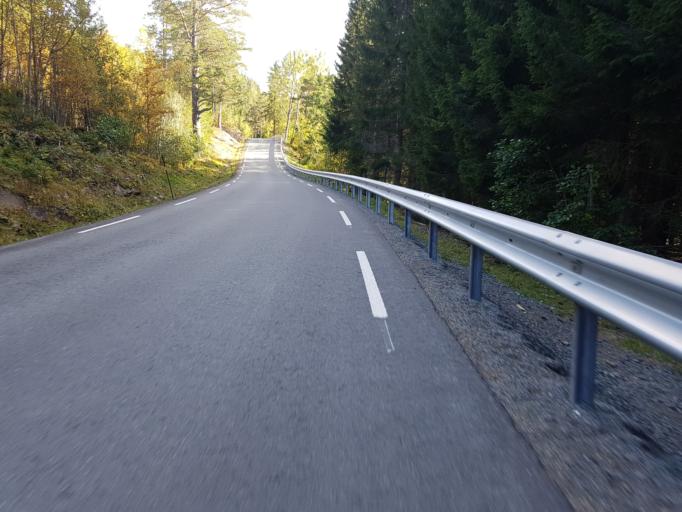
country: NO
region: Sor-Trondelag
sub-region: Malvik
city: Malvik
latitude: 63.3688
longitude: 10.6168
